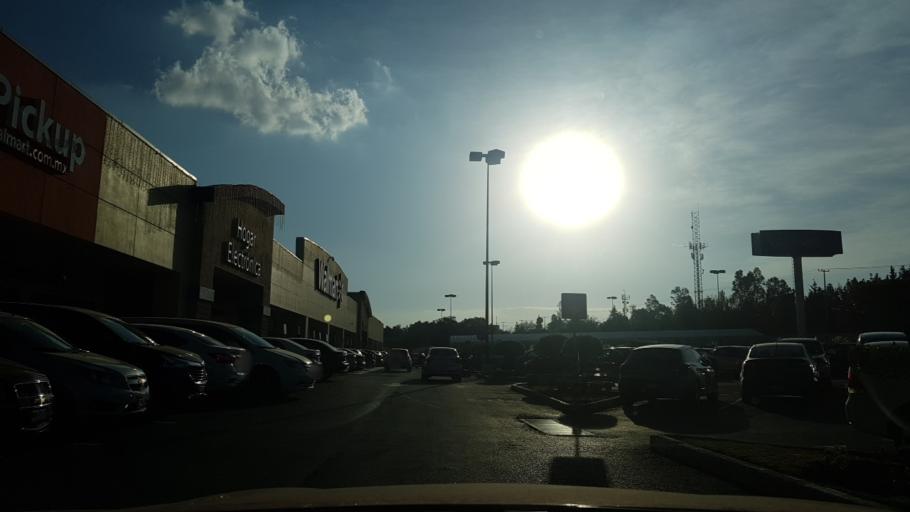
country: MX
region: Mexico
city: Cuautitlan Izcalli
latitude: 19.6394
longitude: -99.2232
